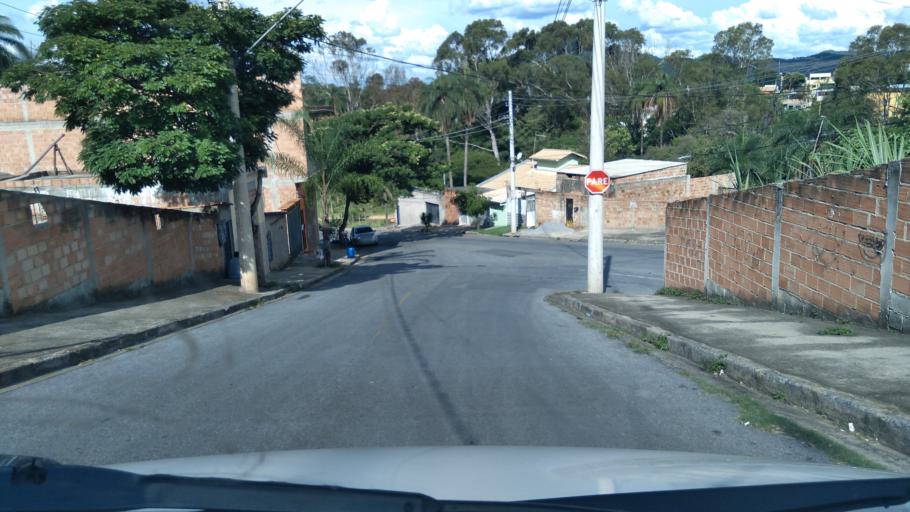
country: BR
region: Minas Gerais
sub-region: Belo Horizonte
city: Belo Horizonte
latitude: -19.8566
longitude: -43.8775
